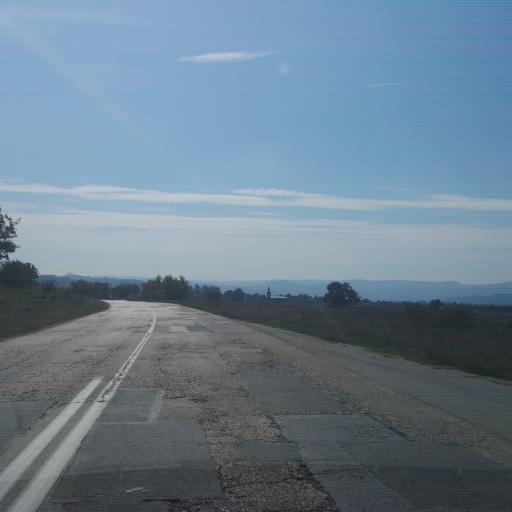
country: RS
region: Central Serbia
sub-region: Zajecarski Okrug
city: Knjazevac
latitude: 43.6336
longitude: 22.2819
